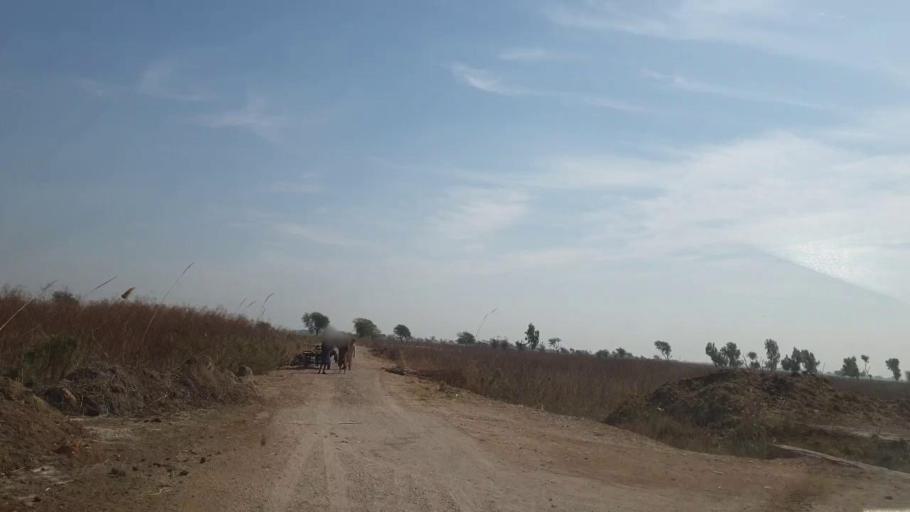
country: PK
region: Sindh
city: Mirpur Khas
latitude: 25.5760
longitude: 69.1881
